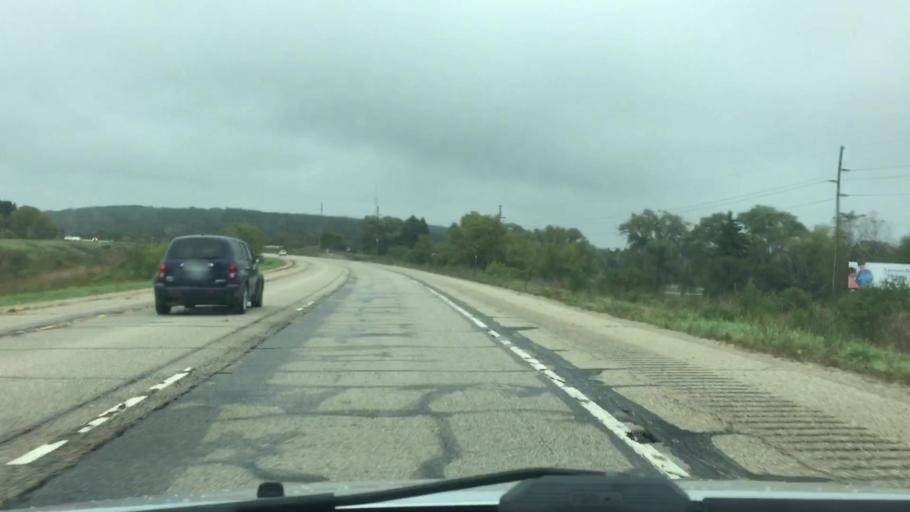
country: US
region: Wisconsin
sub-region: Walworth County
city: Como
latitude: 42.6174
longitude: -88.4581
